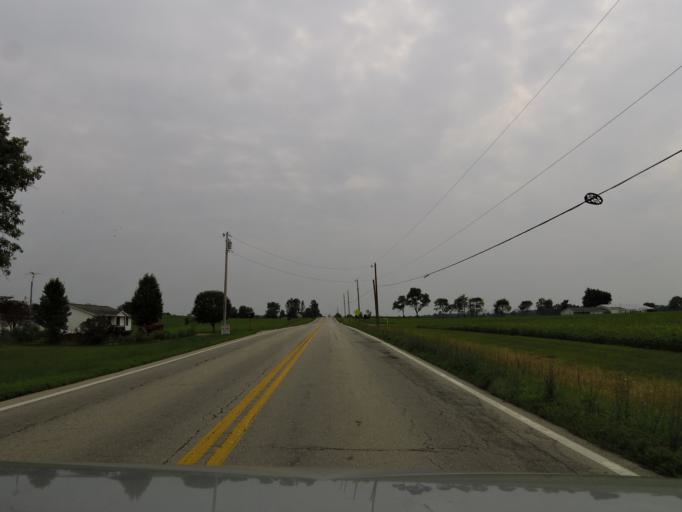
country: US
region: Ohio
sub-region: Clinton County
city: Blanchester
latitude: 39.3341
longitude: -83.8953
